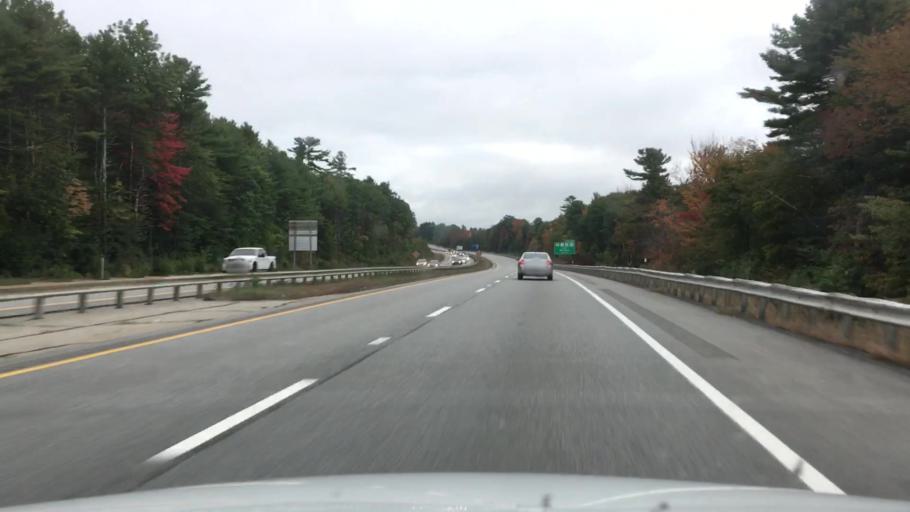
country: US
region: Maine
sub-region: Cumberland County
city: Cumberland Center
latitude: 43.8508
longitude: -70.3229
